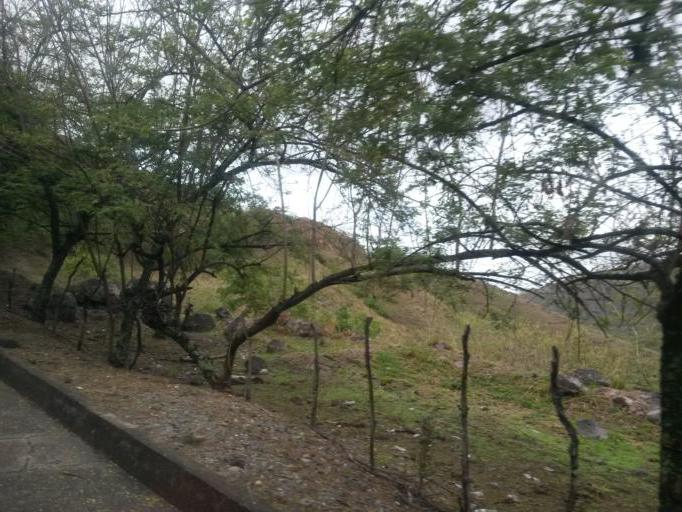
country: CO
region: Cauca
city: El Bordo
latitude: 2.1710
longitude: -76.8941
